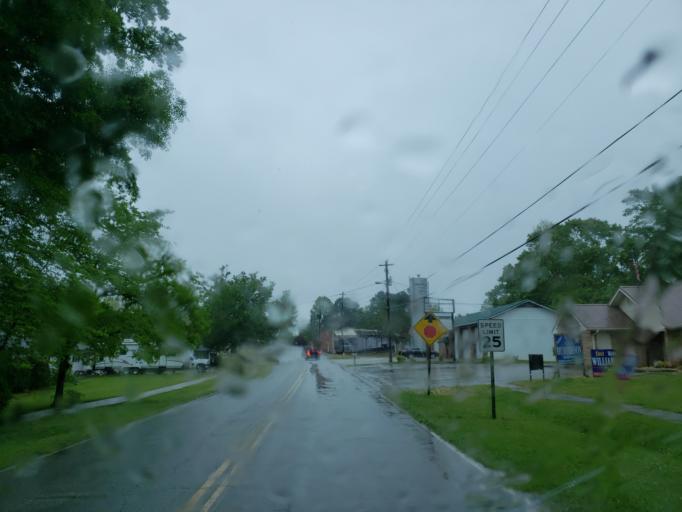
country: US
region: Georgia
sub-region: Haralson County
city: Bremen
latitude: 33.7013
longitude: -85.1845
